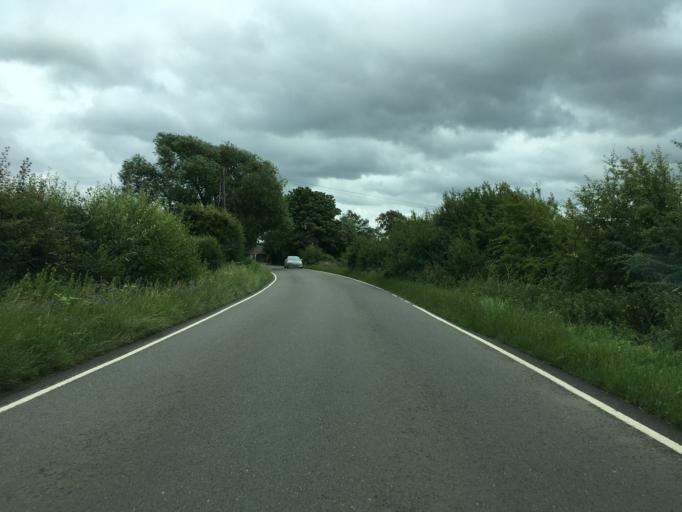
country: GB
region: England
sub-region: Warwickshire
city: Shipston on Stour
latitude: 52.0926
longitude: -1.6817
